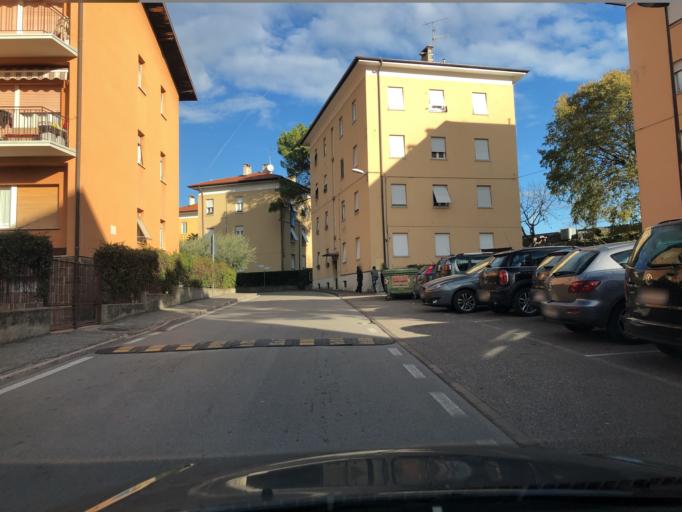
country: IT
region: Trentino-Alto Adige
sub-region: Provincia di Trento
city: Riva del Garda
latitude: 45.8936
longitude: 10.8511
